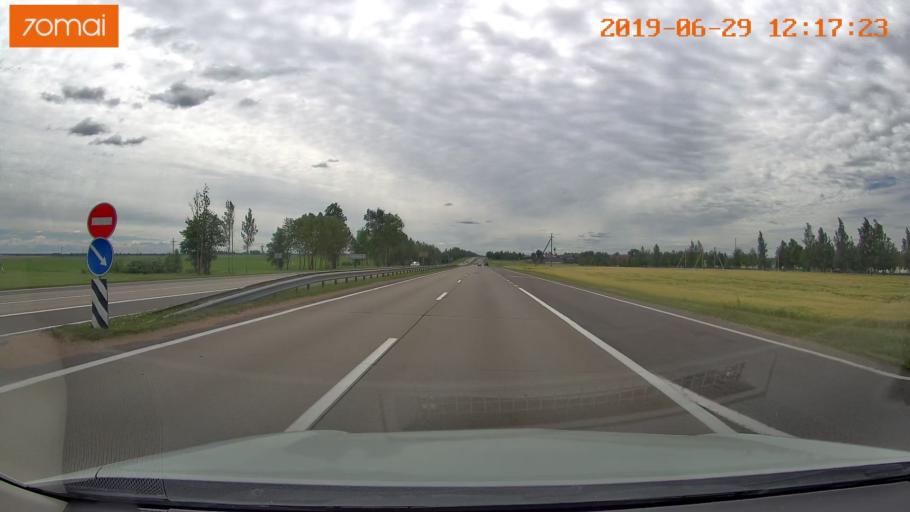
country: BY
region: Minsk
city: Samakhvalavichy
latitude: 53.5896
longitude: 27.4660
